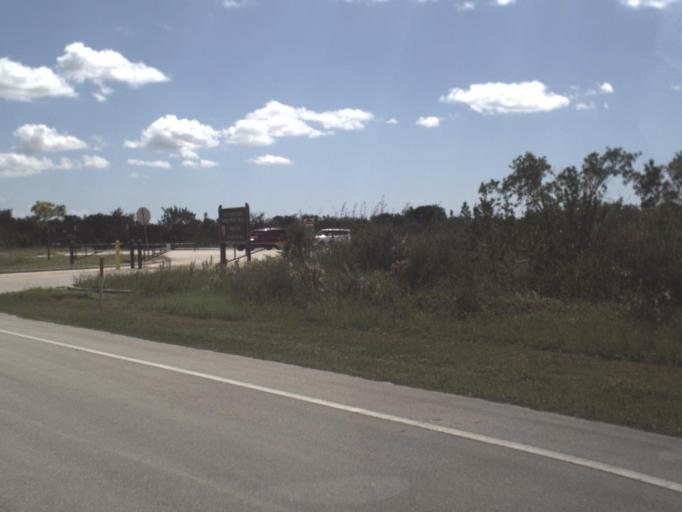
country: US
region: Florida
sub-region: Collier County
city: Marco
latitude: 25.9751
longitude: -81.5547
